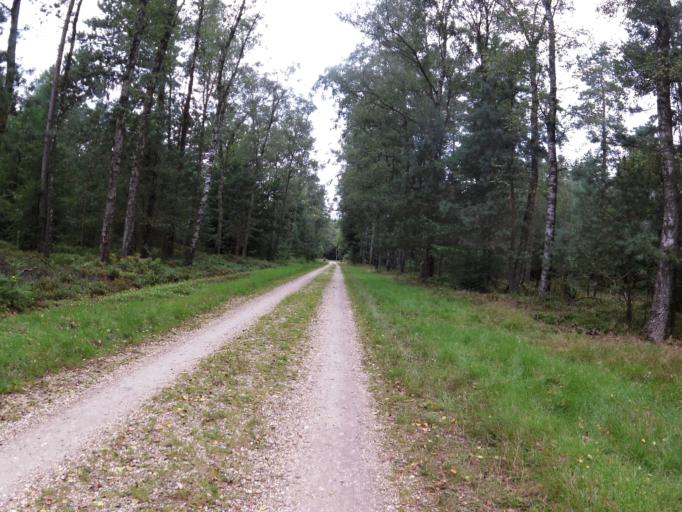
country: NL
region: Gelderland
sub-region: Gemeente Apeldoorn
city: Loenen
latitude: 52.0881
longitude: 6.0105
